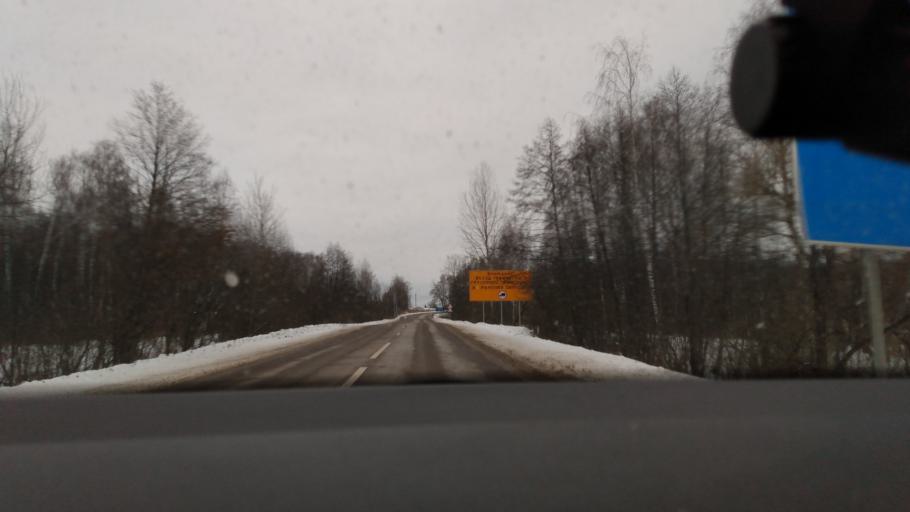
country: RU
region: Moskovskaya
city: Krasnaya Poyma
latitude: 55.1784
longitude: 39.1335
